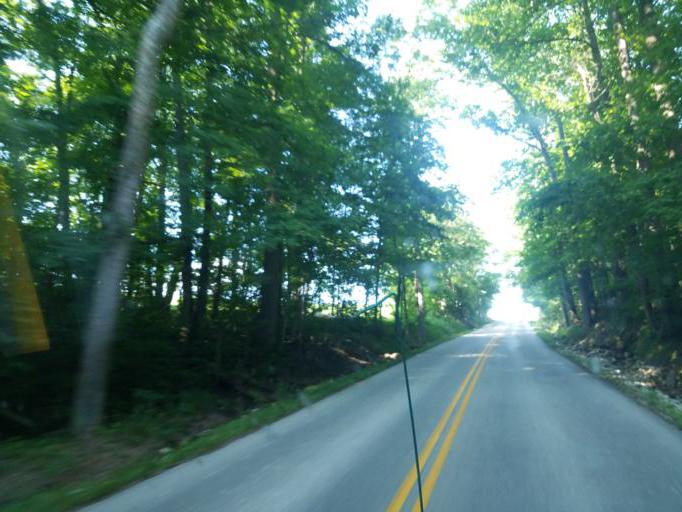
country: US
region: Kentucky
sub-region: Hart County
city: Munfordville
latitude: 37.3372
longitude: -86.0563
